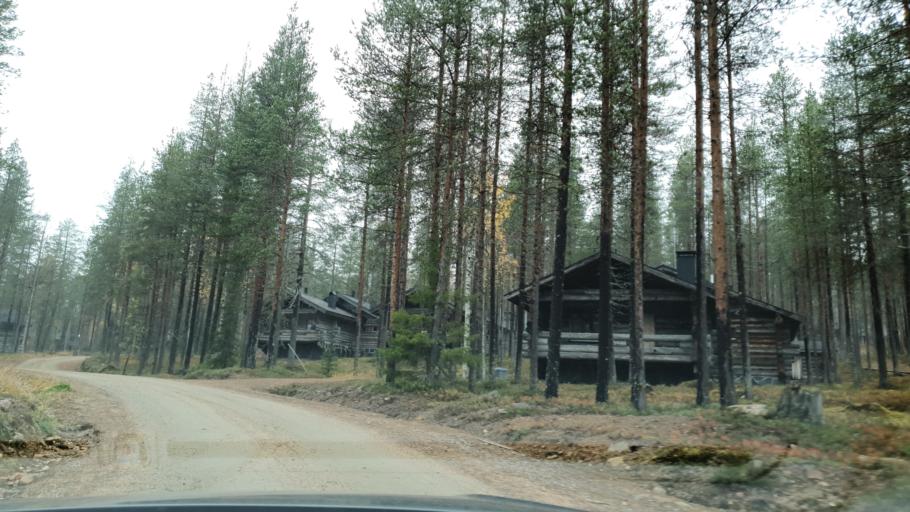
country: FI
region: Lapland
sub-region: Tunturi-Lappi
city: Kolari
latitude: 67.5981
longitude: 24.1171
